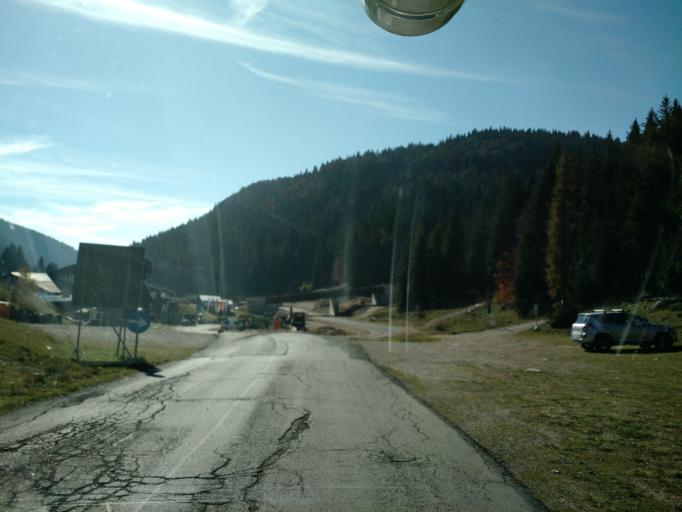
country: IT
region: Veneto
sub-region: Provincia di Vicenza
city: Gallio
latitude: 45.9213
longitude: 11.5610
